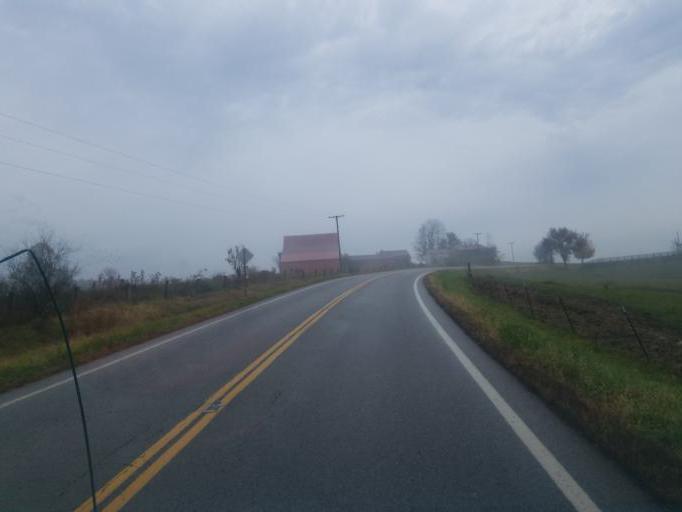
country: US
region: Ohio
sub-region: Morgan County
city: McConnelsville
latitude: 39.4755
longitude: -81.8773
